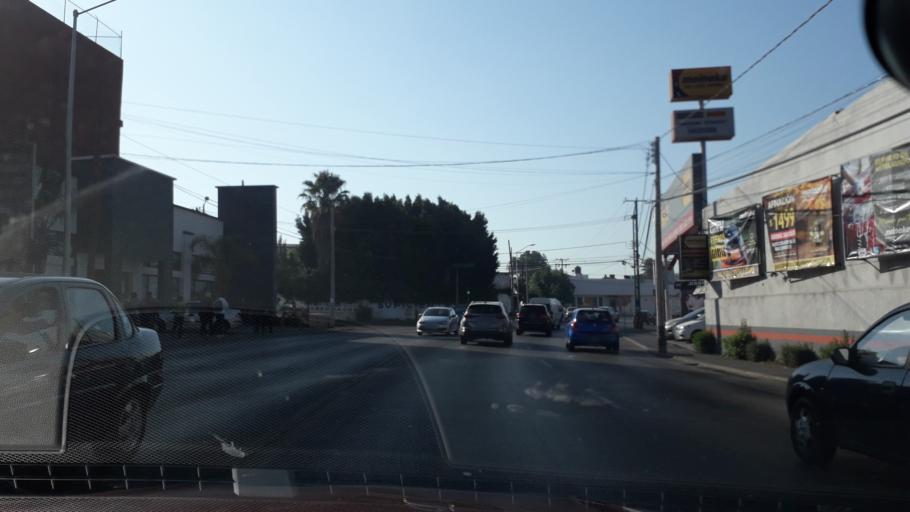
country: MX
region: Puebla
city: Puebla
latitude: 19.0311
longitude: -98.2230
